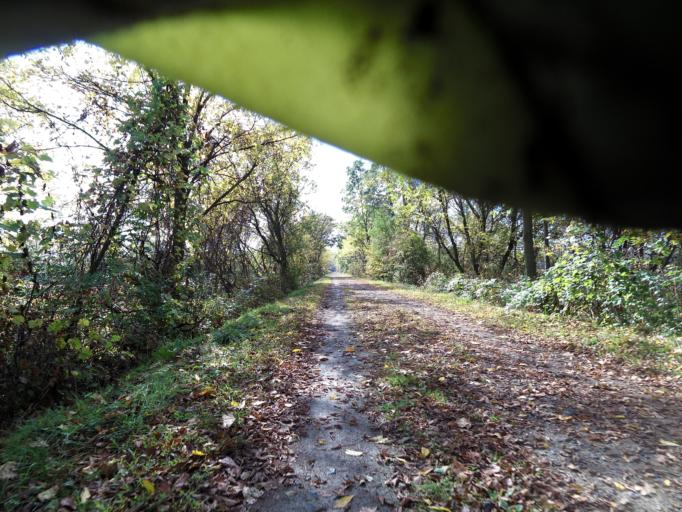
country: CA
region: Ontario
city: Brantford
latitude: 43.1621
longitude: -80.1830
